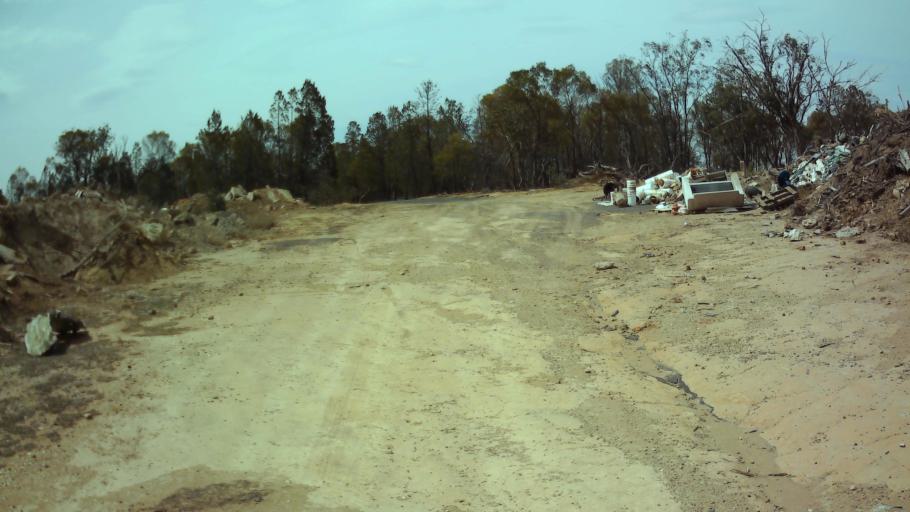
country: AU
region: New South Wales
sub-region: Weddin
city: Grenfell
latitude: -33.8674
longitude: 148.1661
